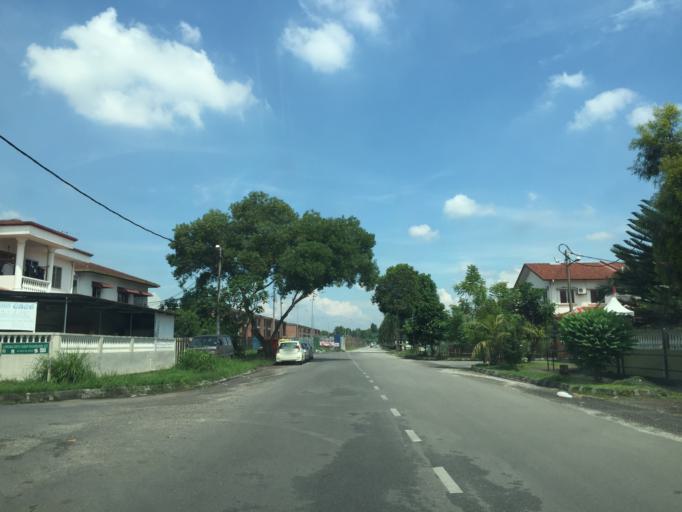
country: MY
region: Selangor
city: Klang
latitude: 3.0056
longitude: 101.4714
